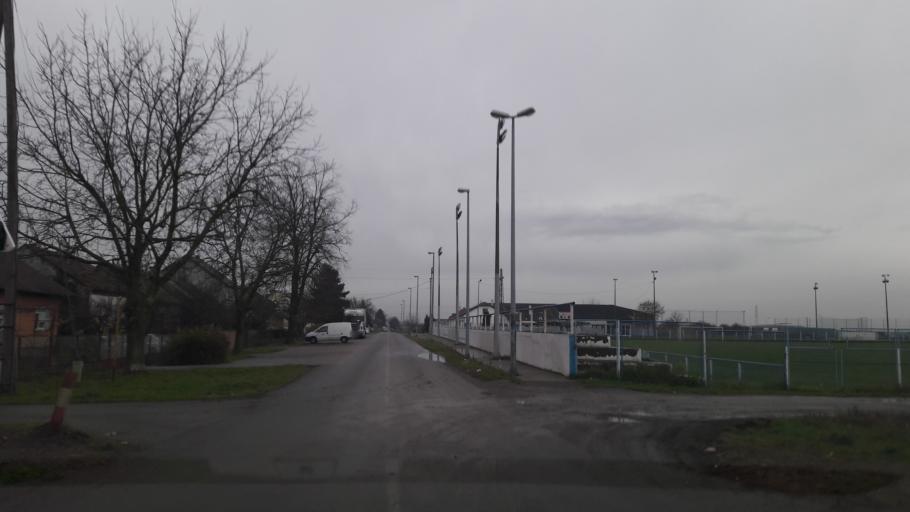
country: HR
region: Osjecko-Baranjska
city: Visnjevac
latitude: 45.5617
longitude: 18.6186
